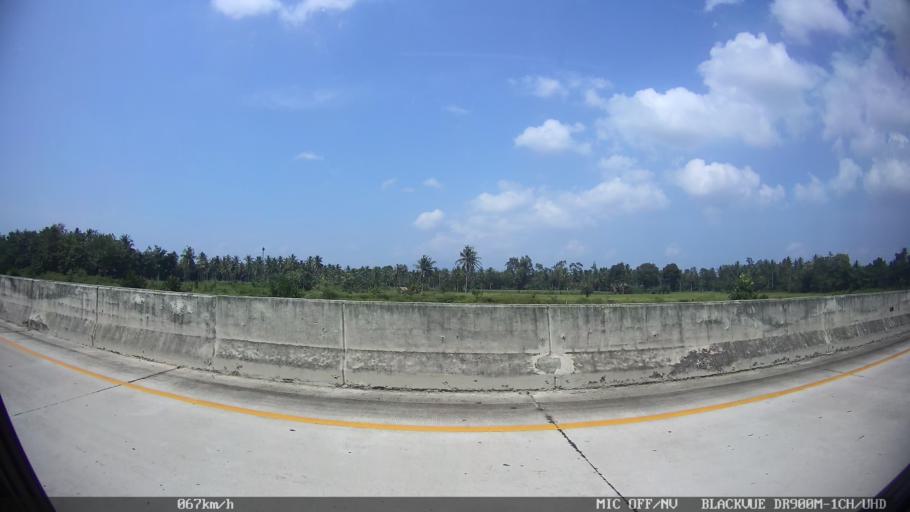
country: ID
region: Lampung
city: Natar
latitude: -5.3066
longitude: 105.2481
